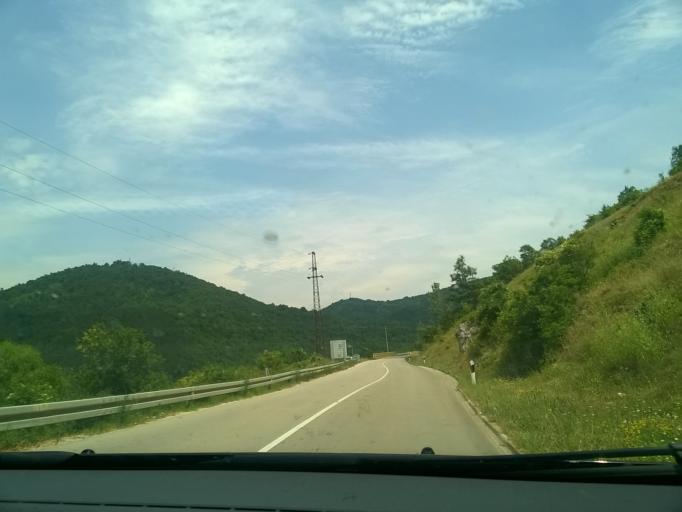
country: RS
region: Central Serbia
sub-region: Nisavski Okrug
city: Aleksinac
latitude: 43.6513
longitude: 21.7149
